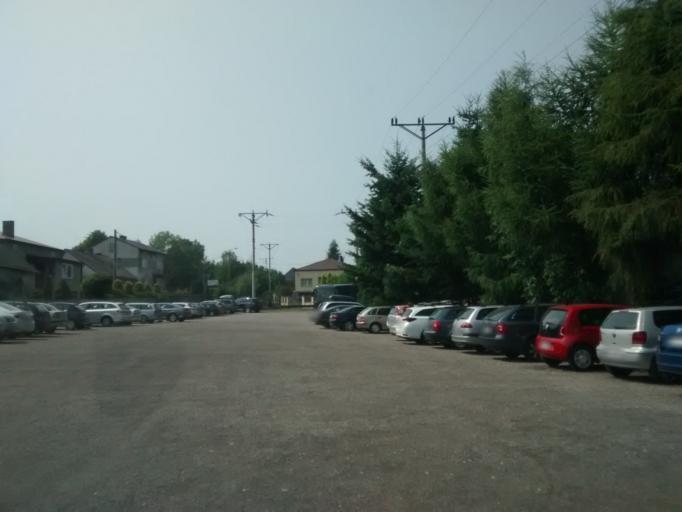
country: PL
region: Silesian Voivodeship
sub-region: Powiat zawiercianski
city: Ogrodzieniec
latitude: 50.4535
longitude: 19.5475
